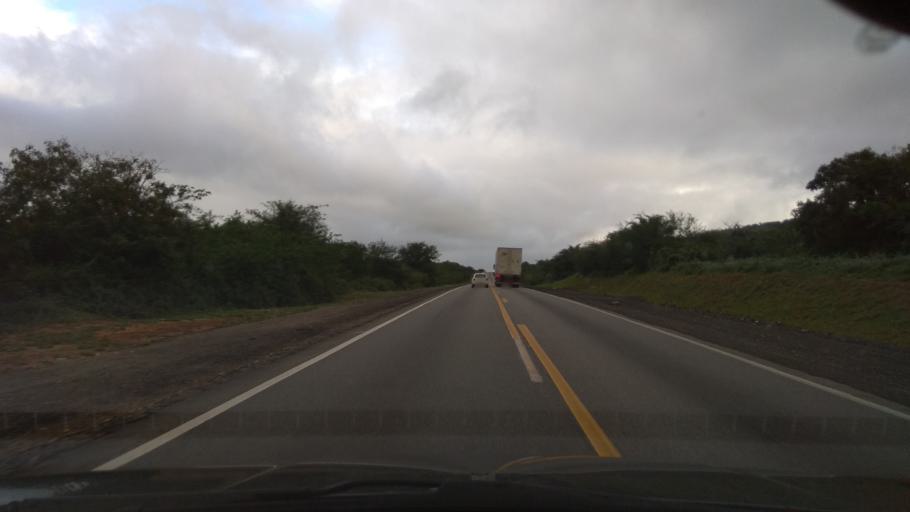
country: BR
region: Bahia
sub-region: Jaguaquara
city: Jaguaquara
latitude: -13.3463
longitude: -40.0166
